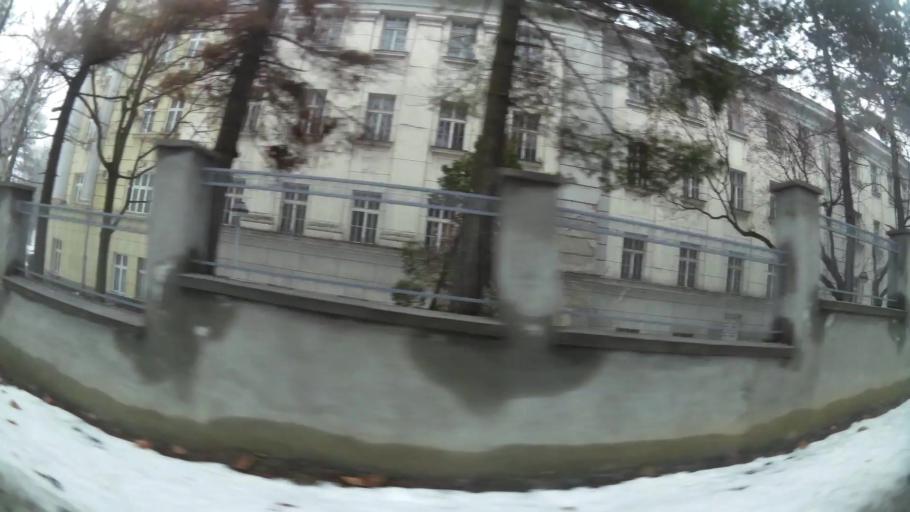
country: RS
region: Central Serbia
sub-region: Belgrade
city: Vozdovac
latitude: 44.7759
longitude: 20.4679
